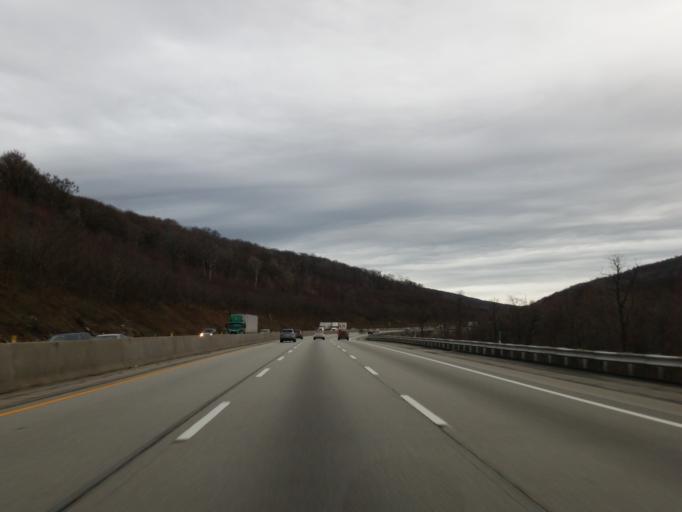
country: US
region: Pennsylvania
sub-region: Westmoreland County
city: Ligonier
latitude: 40.1179
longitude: -79.2660
